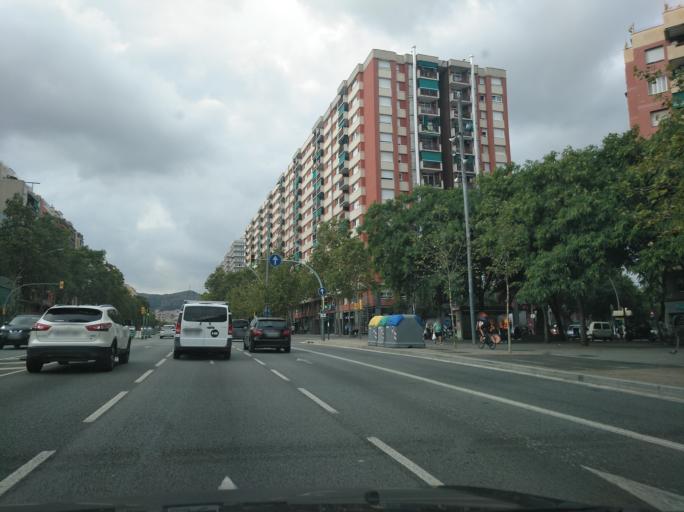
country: ES
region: Catalonia
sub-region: Provincia de Barcelona
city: Sant Andreu de Palomar
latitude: 41.4252
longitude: 2.1865
